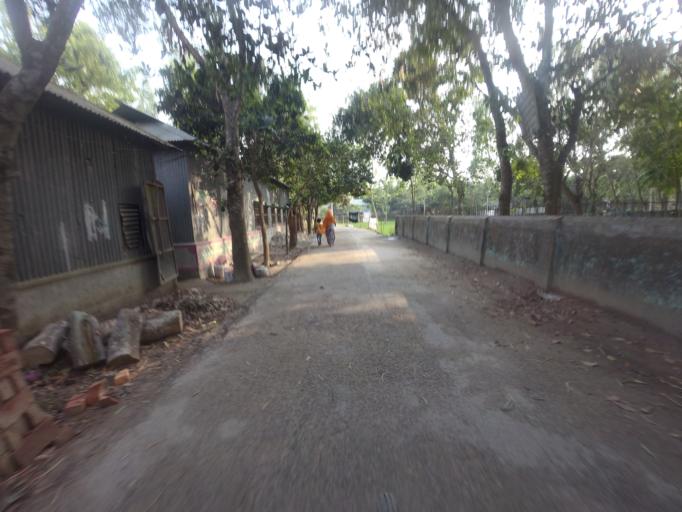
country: BD
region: Rajshahi
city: Sirajganj
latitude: 24.3291
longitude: 89.7147
